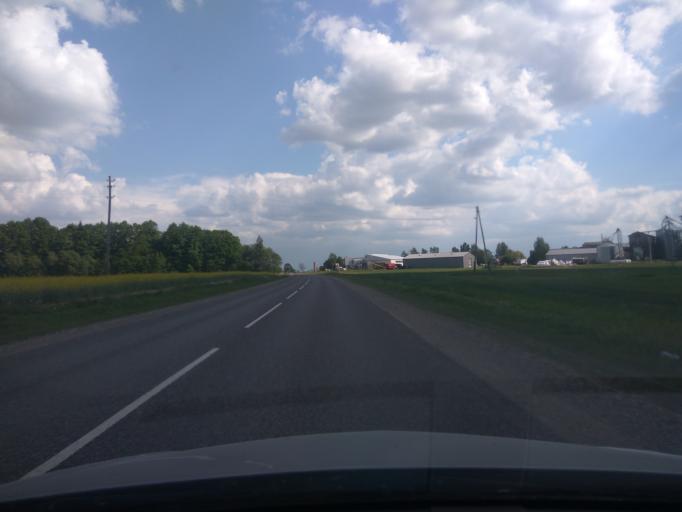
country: LV
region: Kuldigas Rajons
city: Kuldiga
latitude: 57.0010
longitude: 21.8971
